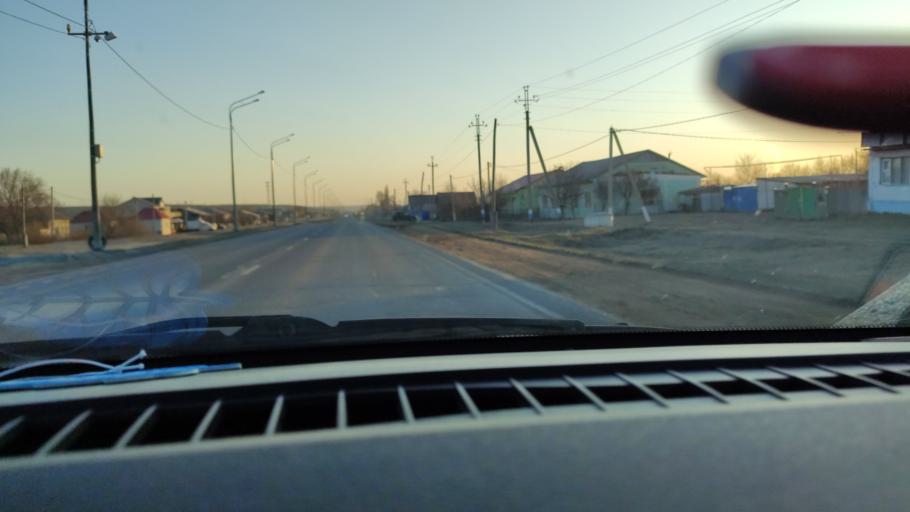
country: RU
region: Saratov
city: Sinodskoye
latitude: 51.9900
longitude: 46.6678
